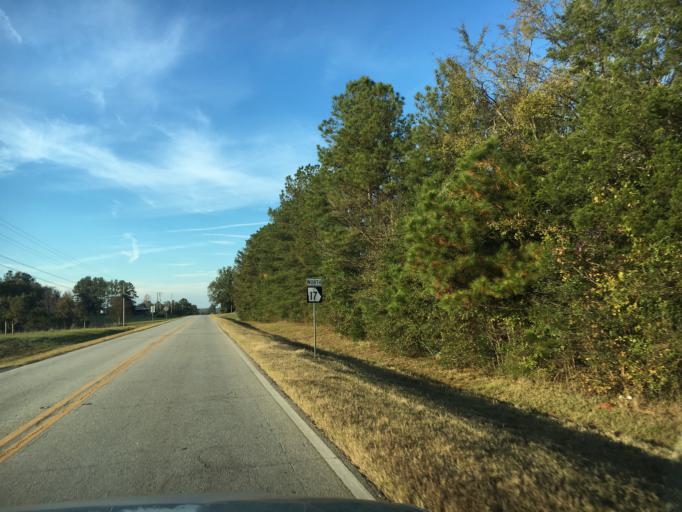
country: US
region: Georgia
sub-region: Elbert County
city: Elberton
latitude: 34.0233
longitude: -82.7913
